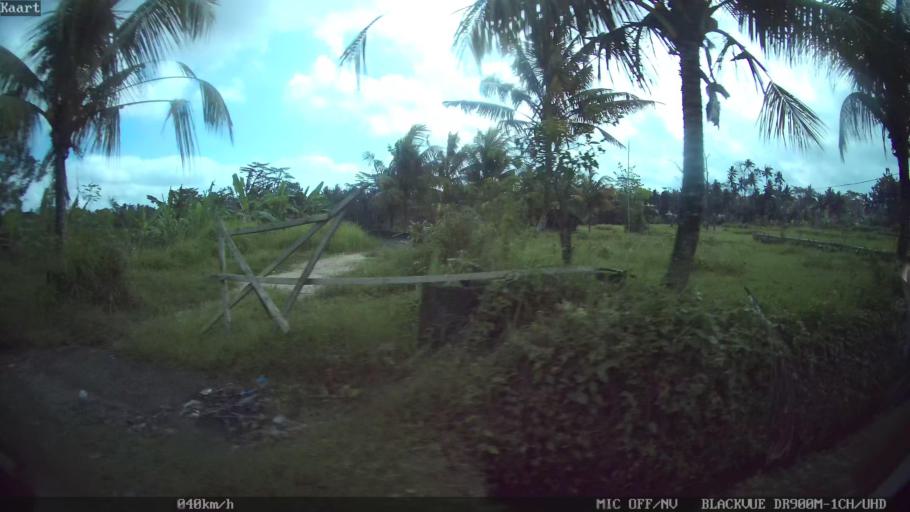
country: ID
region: Bali
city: Banjar Pesalakan
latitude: -8.4975
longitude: 115.3047
